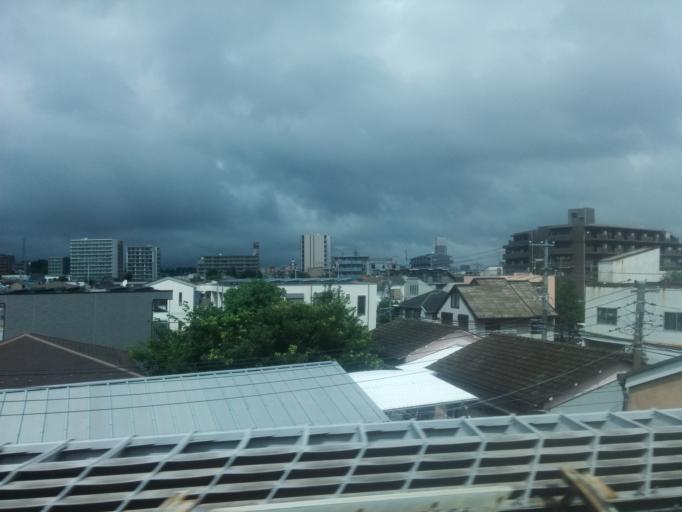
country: JP
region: Kanagawa
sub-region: Kawasaki-shi
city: Kawasaki
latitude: 35.5574
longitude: 139.6572
